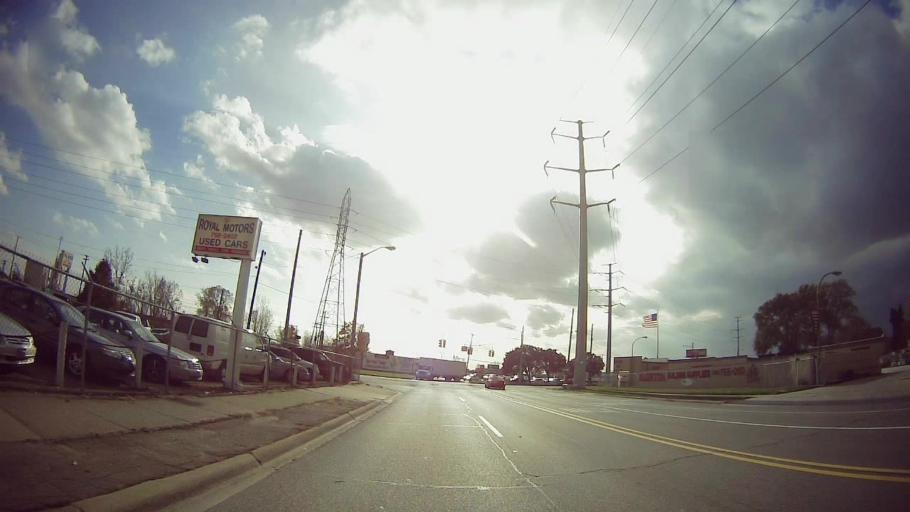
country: US
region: Michigan
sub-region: Macomb County
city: Warren
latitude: 42.4495
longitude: -83.0061
